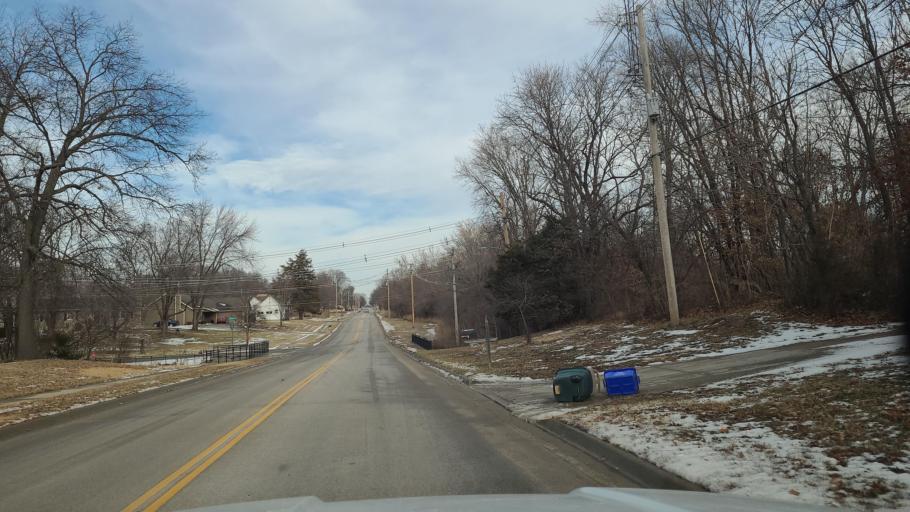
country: US
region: Kansas
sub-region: Douglas County
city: Baldwin City
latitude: 38.7681
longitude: -95.1860
